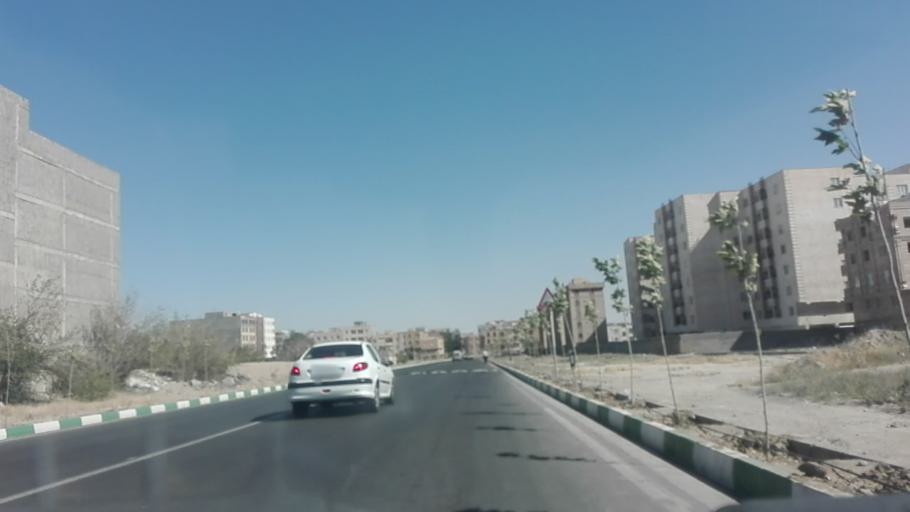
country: IR
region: Tehran
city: Shahriar
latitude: 35.6504
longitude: 51.0586
